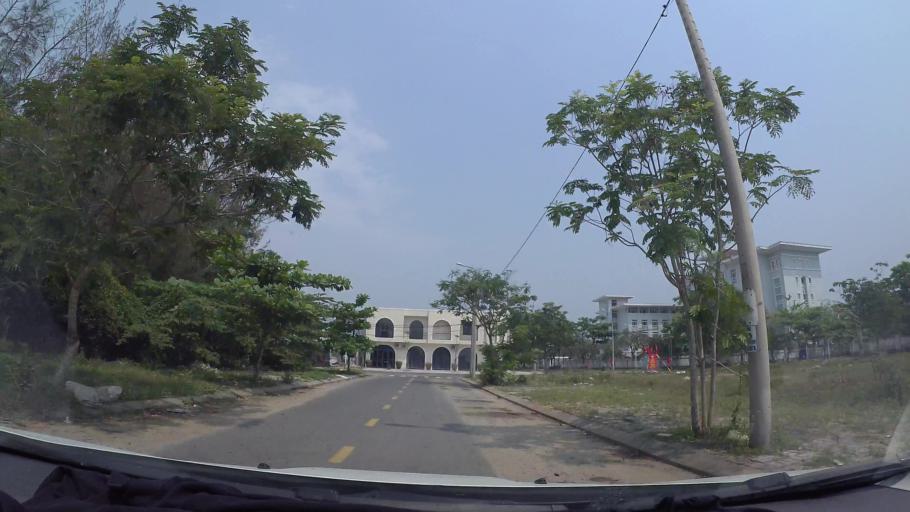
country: VN
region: Da Nang
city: Cam Le
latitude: 15.9975
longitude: 108.2104
